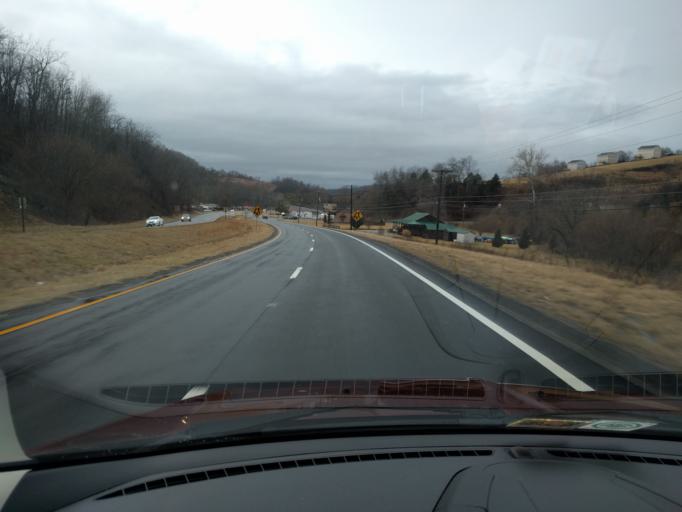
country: US
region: Virginia
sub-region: Giles County
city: Pembroke
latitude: 37.3195
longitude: -80.6133
